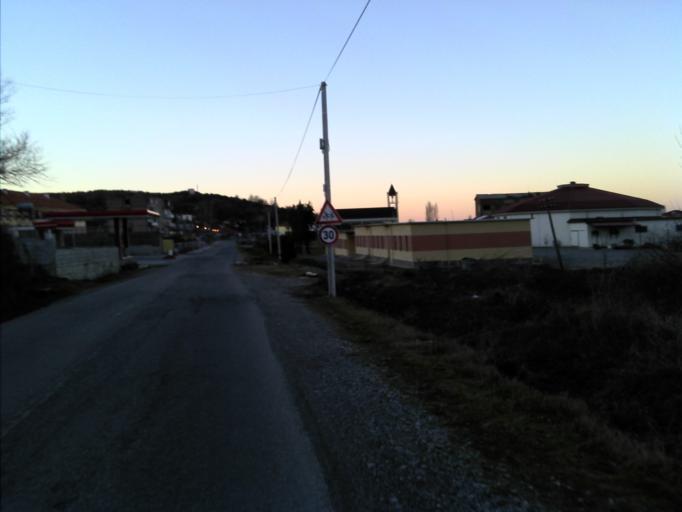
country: AL
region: Shkoder
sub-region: Rrethi i Shkodres
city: Berdica e Madhe
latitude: 42.0189
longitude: 19.4849
